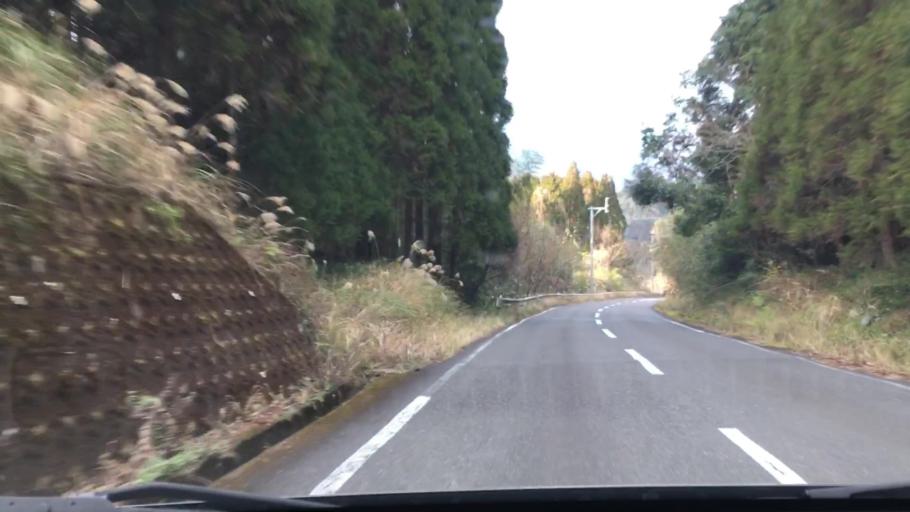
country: JP
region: Miyazaki
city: Nichinan
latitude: 31.6072
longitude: 131.3299
